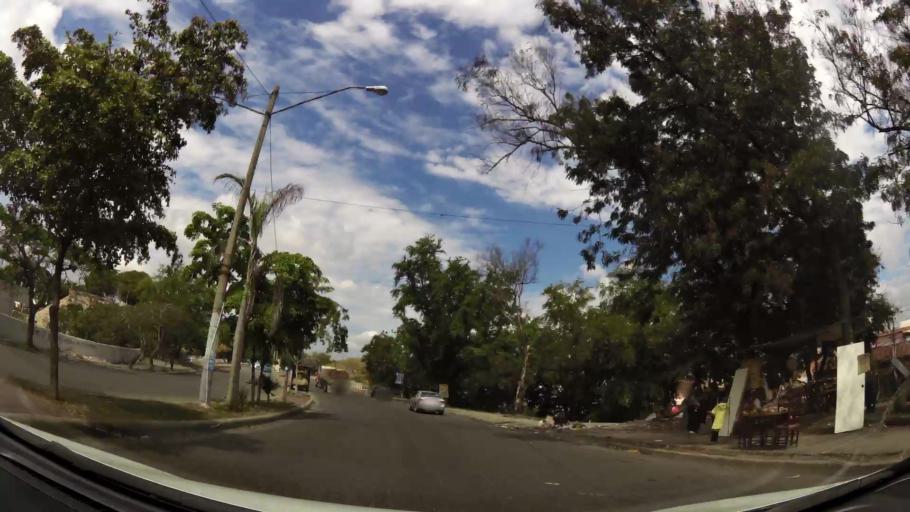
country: DO
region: Santiago
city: Santiago de los Caballeros
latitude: 19.4572
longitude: -70.7063
